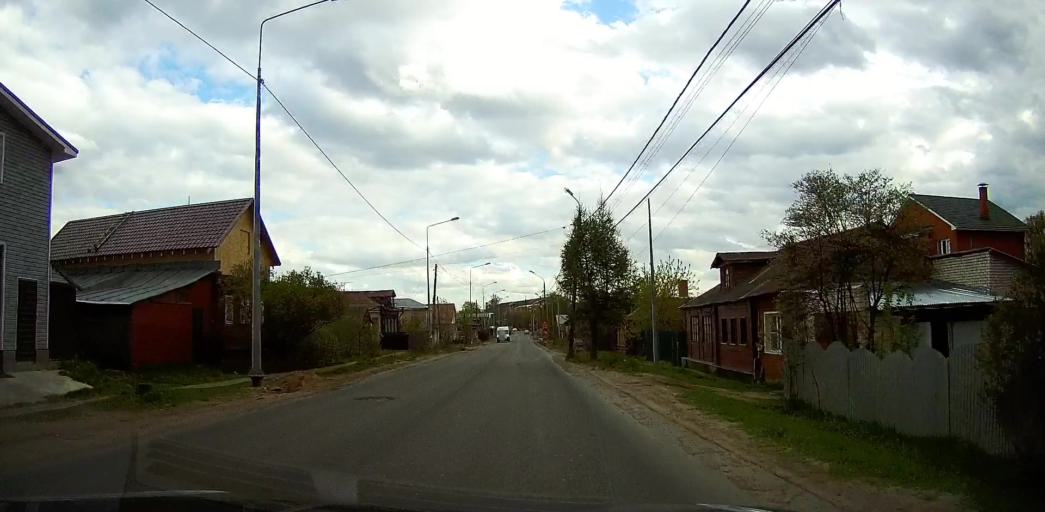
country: RU
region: Moskovskaya
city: Pavlovskiy Posad
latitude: 55.7880
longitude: 38.6859
